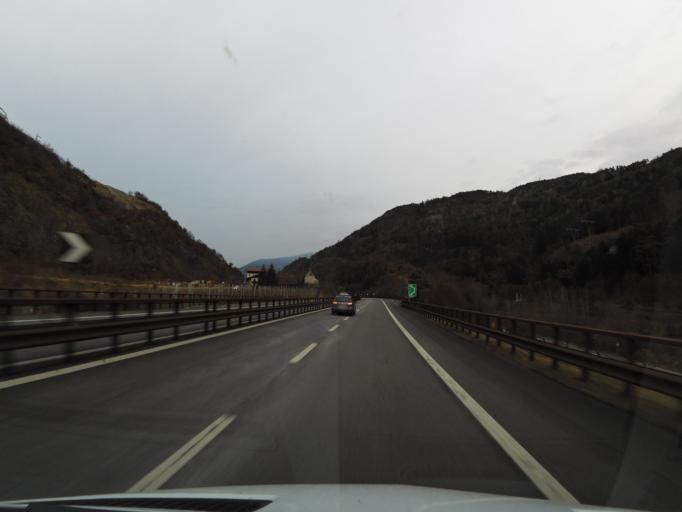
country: IT
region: Trentino-Alto Adige
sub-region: Bolzano
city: Velturno
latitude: 46.6572
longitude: 11.6029
